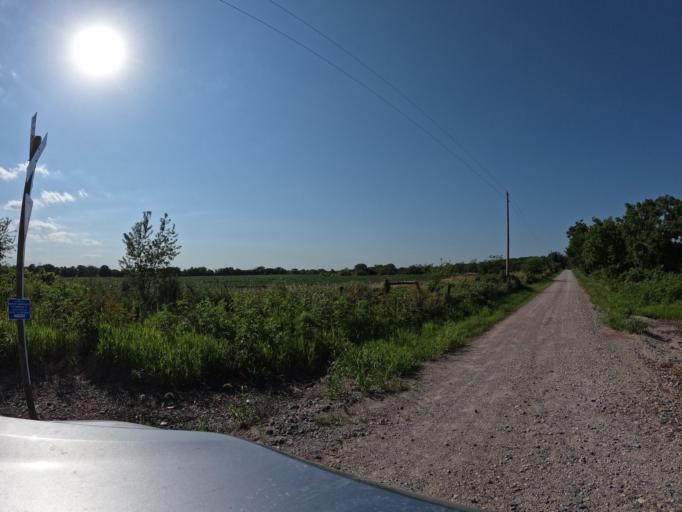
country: US
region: Iowa
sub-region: Appanoose County
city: Centerville
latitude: 40.7262
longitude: -93.0159
